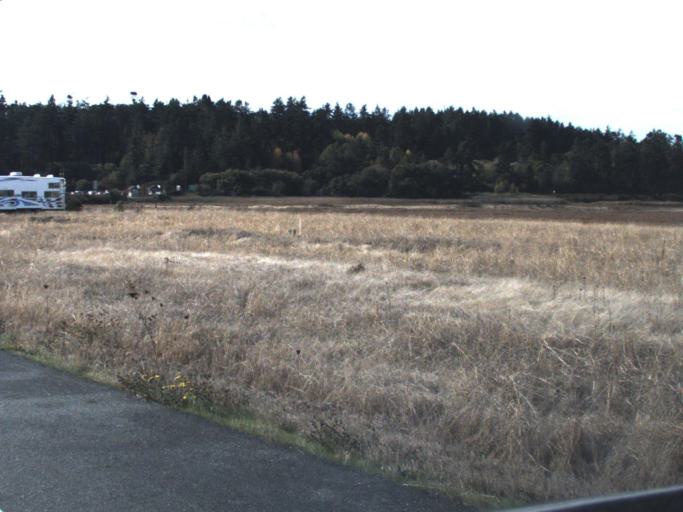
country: US
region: Washington
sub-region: Island County
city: Coupeville
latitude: 48.1602
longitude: -122.6683
